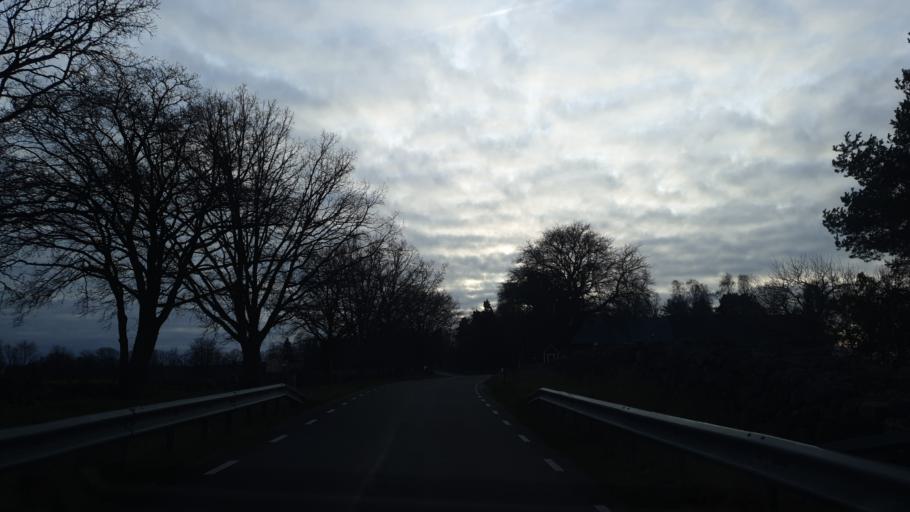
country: SE
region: Blekinge
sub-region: Karlskrona Kommun
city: Jaemjoe
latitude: 56.2280
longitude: 15.9929
